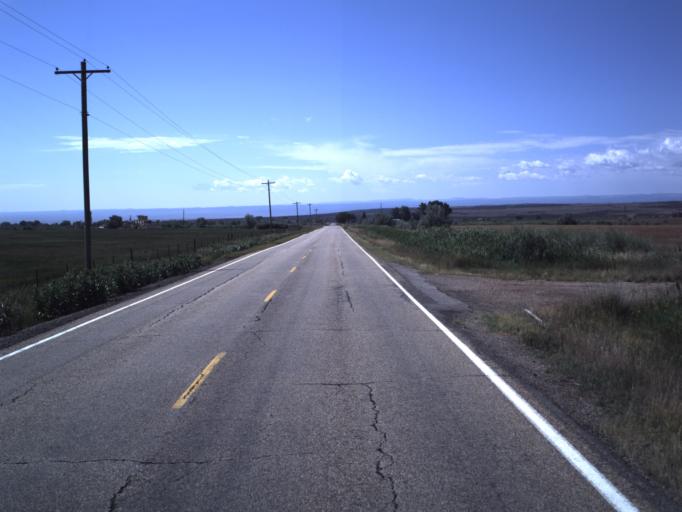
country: US
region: Utah
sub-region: Duchesne County
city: Duchesne
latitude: 40.3403
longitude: -110.2752
